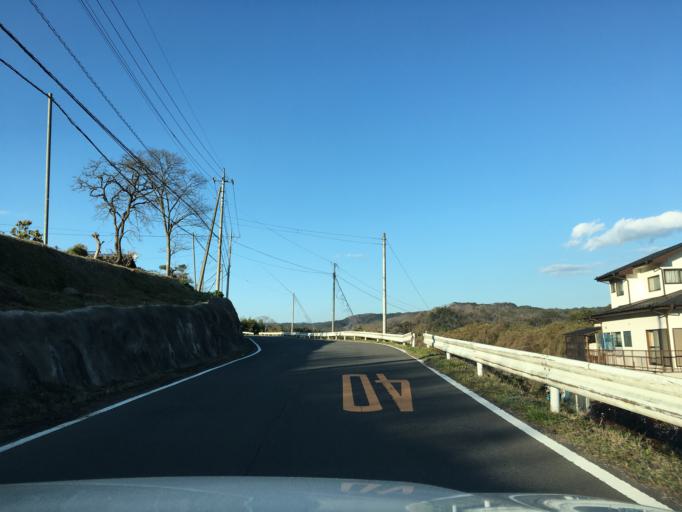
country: JP
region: Tochigi
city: Karasuyama
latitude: 36.7684
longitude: 140.2054
